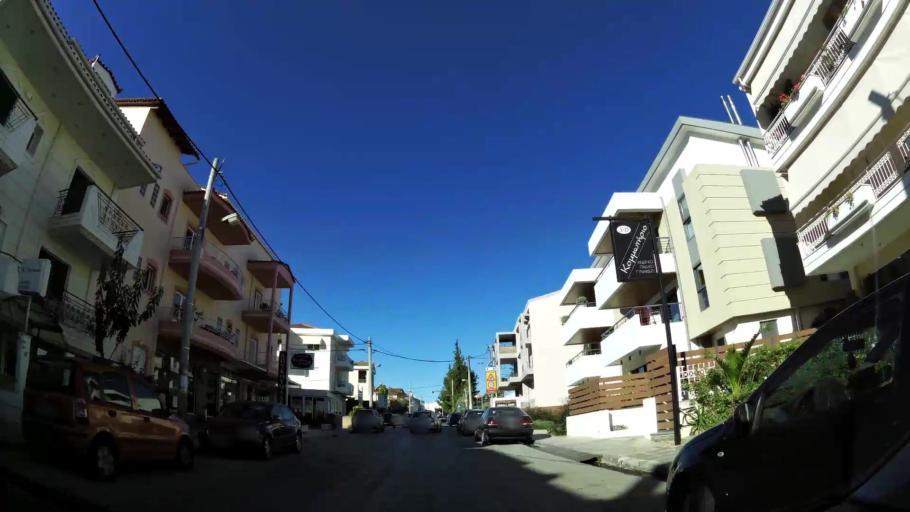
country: GR
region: Attica
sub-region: Nomarchia Anatolikis Attikis
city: Gerakas
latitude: 38.0122
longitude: 23.8478
